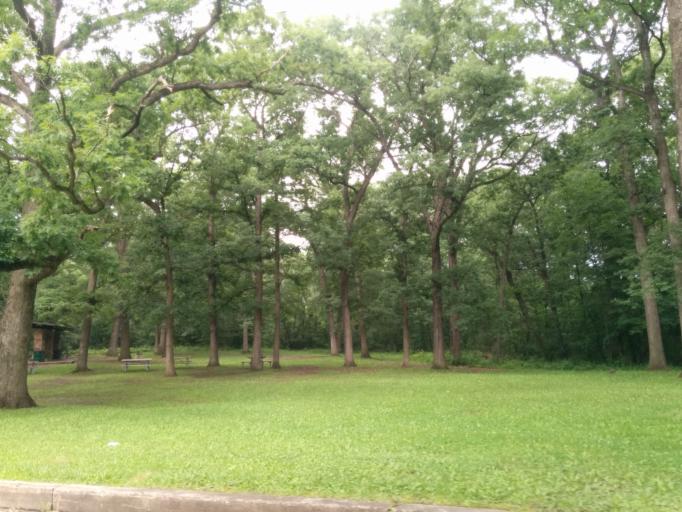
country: US
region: Illinois
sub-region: Cook County
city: Palos Park
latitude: 41.6757
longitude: -87.8382
